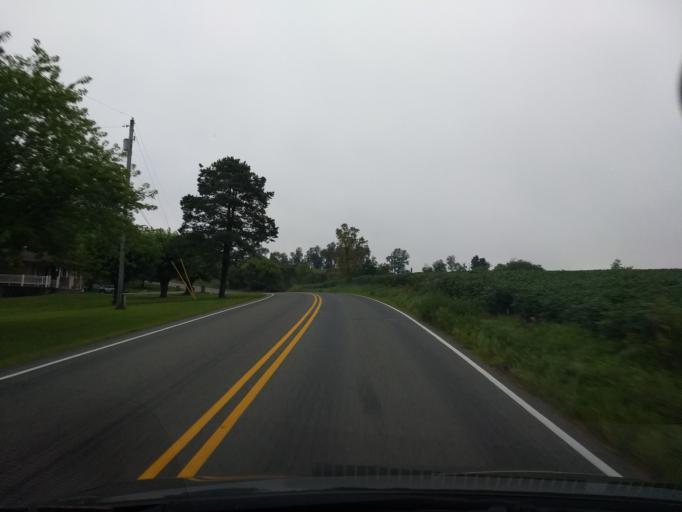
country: US
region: Pennsylvania
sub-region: Westmoreland County
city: Greensburg
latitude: 40.3325
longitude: -79.4875
